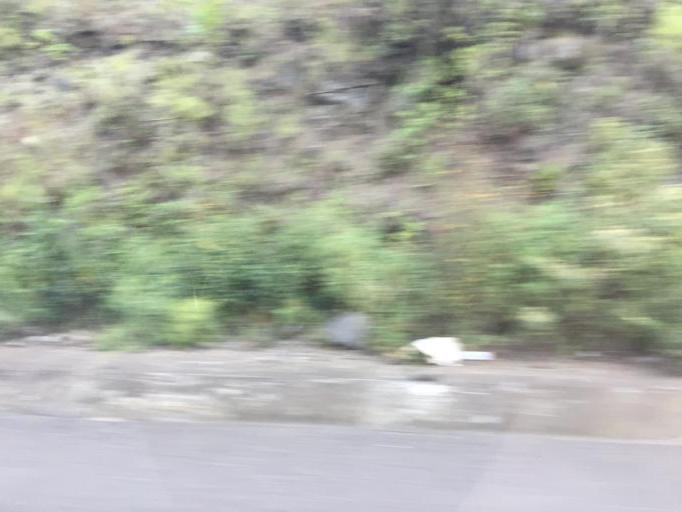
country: MX
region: Michoacan
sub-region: Puruandiro
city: San Lorenzo
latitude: 19.9607
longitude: -101.6755
